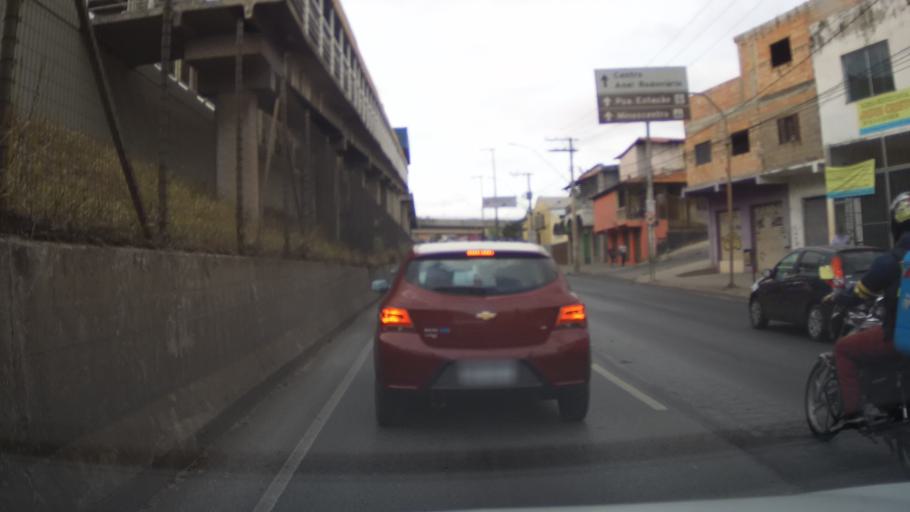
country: BR
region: Minas Gerais
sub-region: Belo Horizonte
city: Belo Horizonte
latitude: -19.8335
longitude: -43.9406
